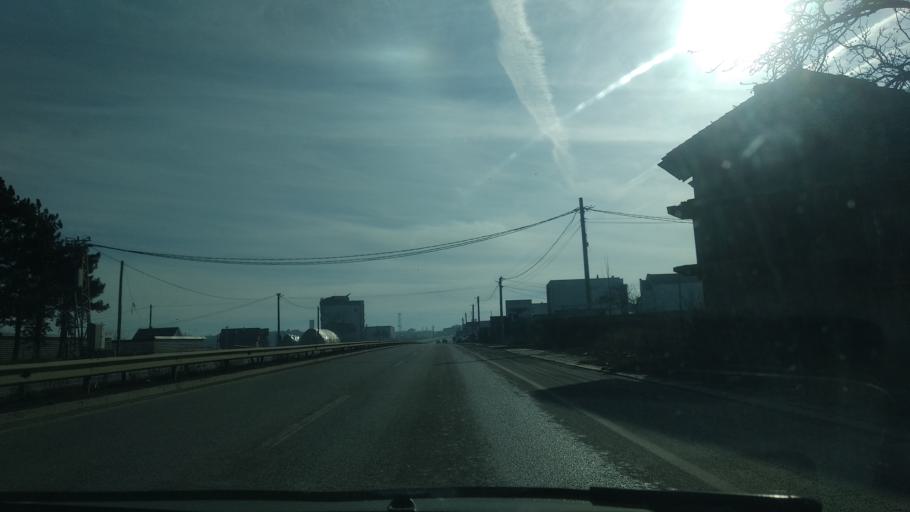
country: XK
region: Pristina
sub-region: Kosovo Polje
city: Kosovo Polje
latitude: 42.6987
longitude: 21.1123
